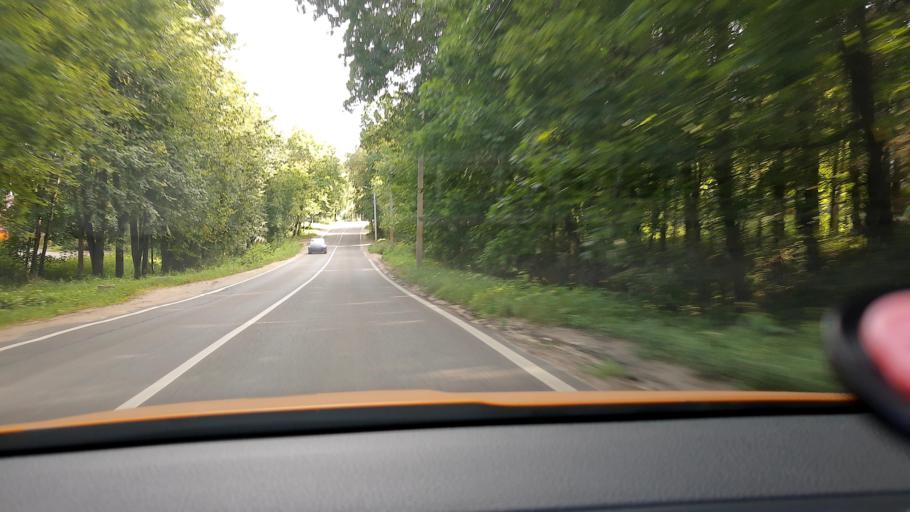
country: RU
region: Moskovskaya
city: Zvenigorod
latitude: 55.7390
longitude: 36.8489
